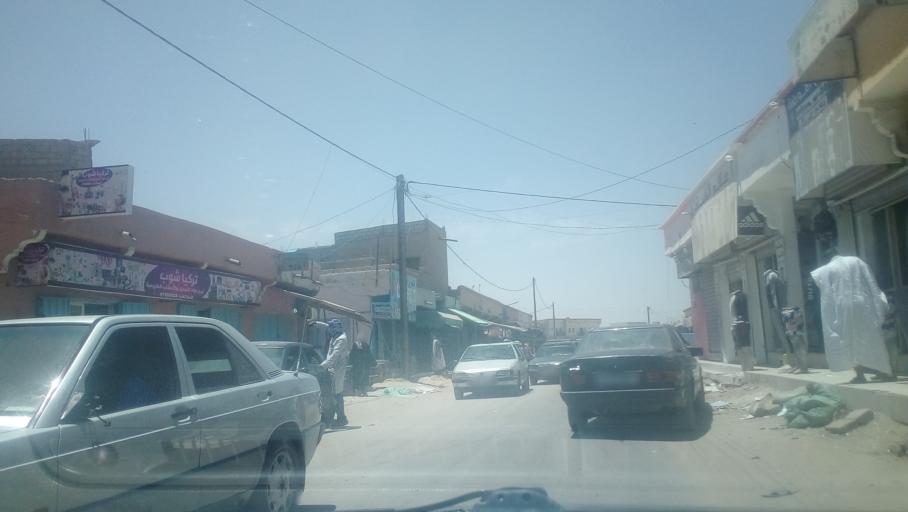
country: MR
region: Nouakchott
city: Nouakchott
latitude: 18.0568
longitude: -15.9615
